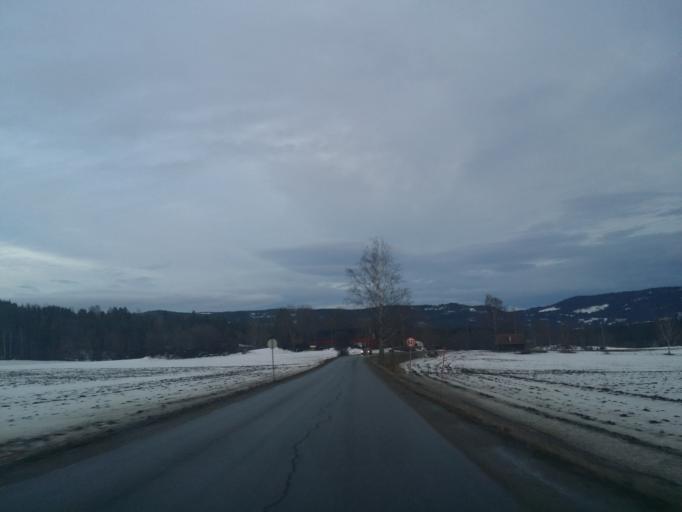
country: NO
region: Buskerud
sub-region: Ringerike
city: Honefoss
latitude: 60.1399
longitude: 10.2930
